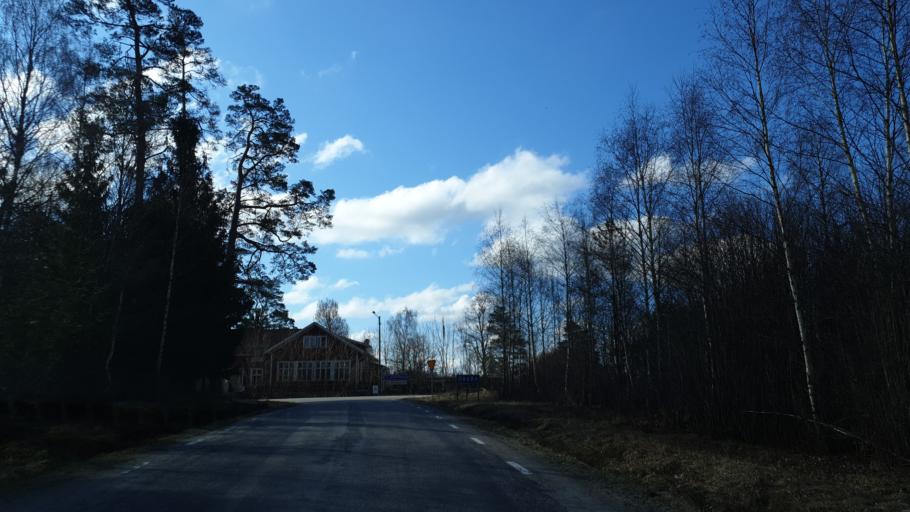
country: SE
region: Vaestra Goetaland
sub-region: Svenljunga Kommun
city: Svenljunga
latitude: 57.4432
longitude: 13.1194
